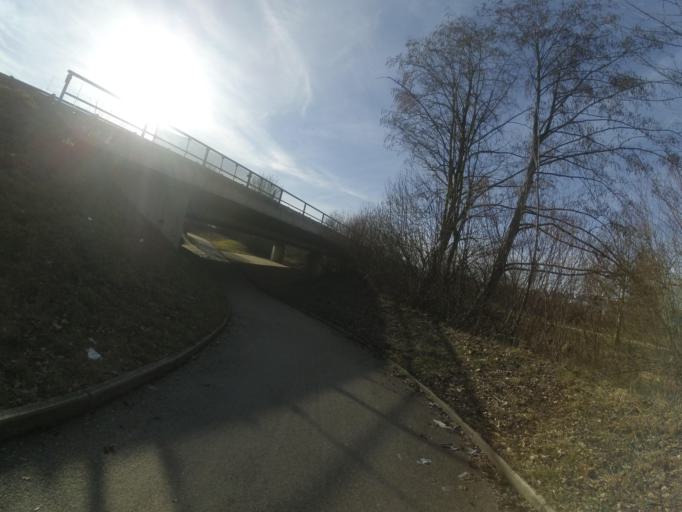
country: DE
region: Baden-Wuerttemberg
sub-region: Regierungsbezirk Stuttgart
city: Herbrechtingen
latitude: 48.6271
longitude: 10.1885
